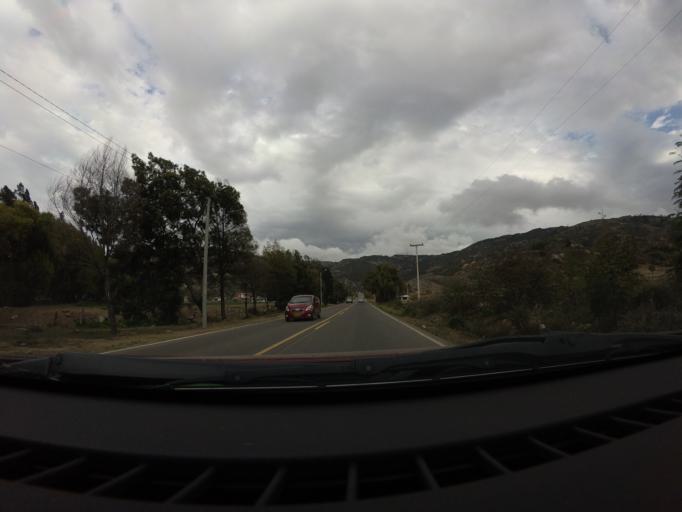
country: CO
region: Boyaca
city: Cucaita
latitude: 5.5406
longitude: -73.4555
